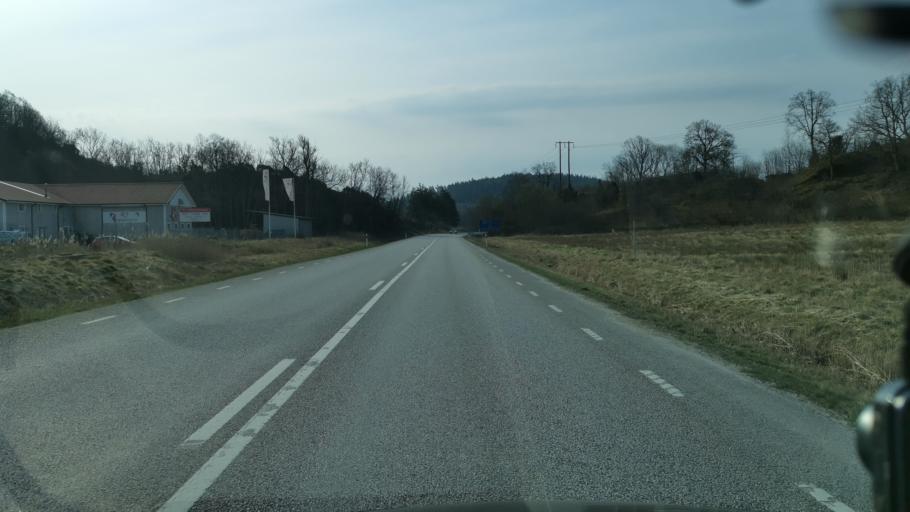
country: SE
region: Vaestra Goetaland
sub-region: Tjorns Kommun
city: Myggenas
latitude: 58.1301
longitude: 11.7214
